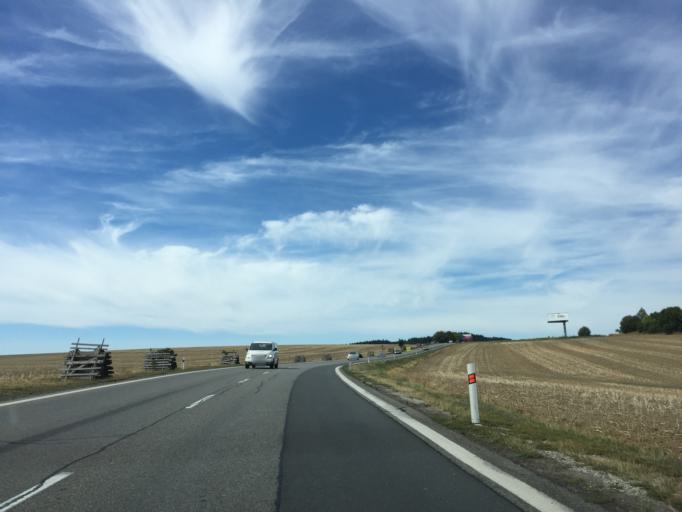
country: CZ
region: Jihocesky
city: Chotoviny
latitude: 49.5589
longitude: 14.6631
